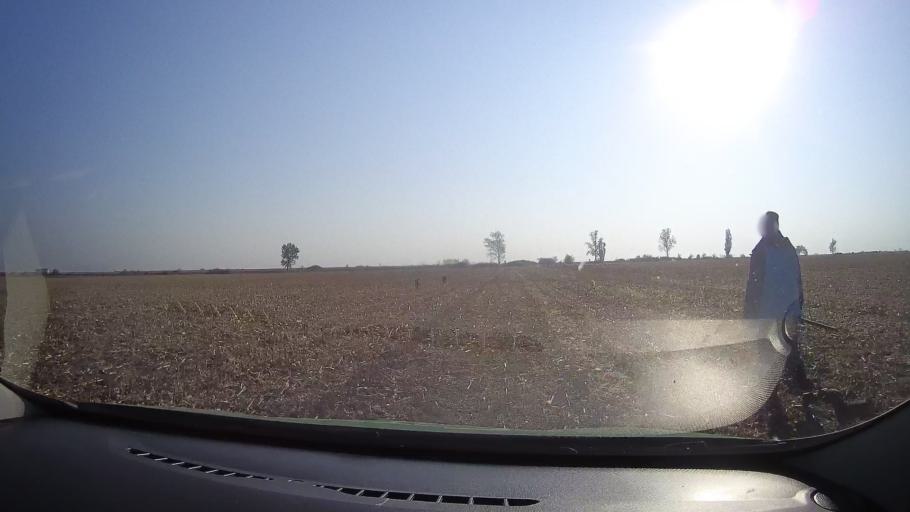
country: RO
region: Arad
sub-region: Comuna Pilu
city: Pilu
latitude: 46.5574
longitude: 21.3439
